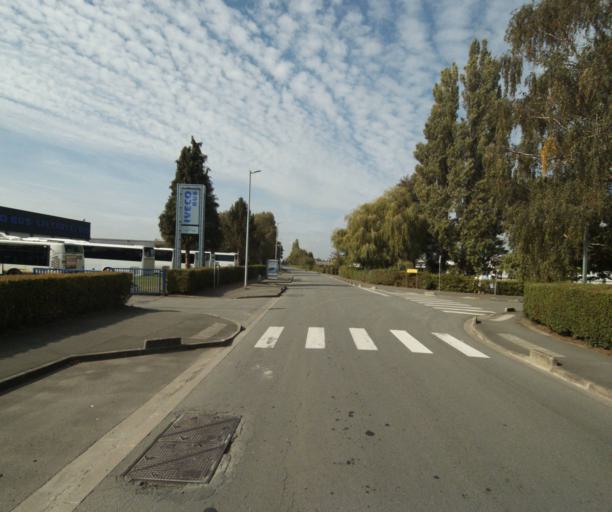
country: FR
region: Nord-Pas-de-Calais
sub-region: Departement du Nord
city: Templemars
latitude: 50.5656
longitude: 3.0392
